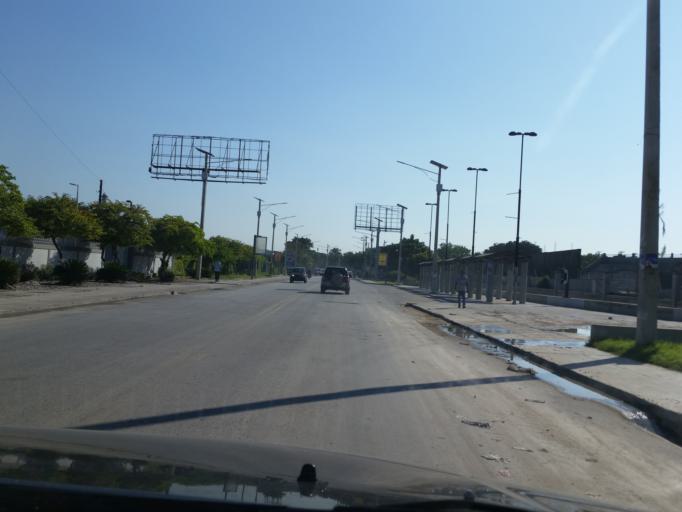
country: HT
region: Ouest
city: Delmas 73
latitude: 18.5751
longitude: -72.2998
